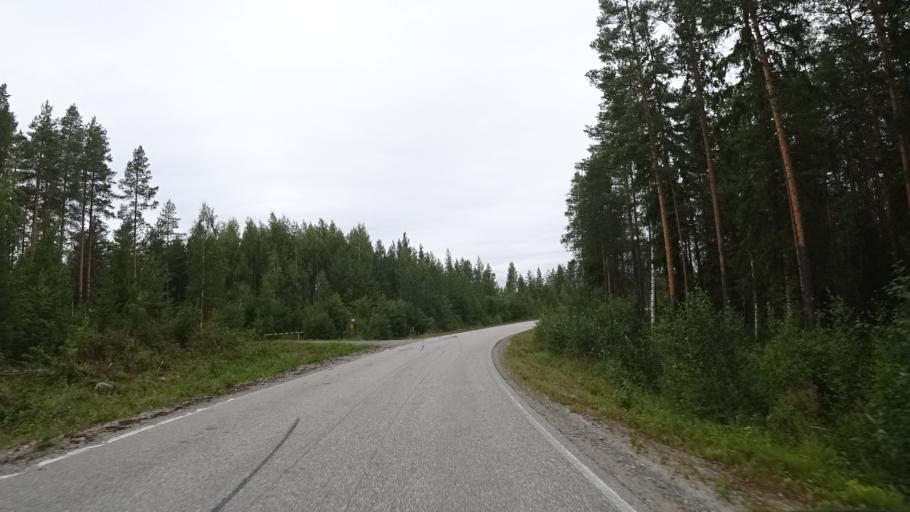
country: FI
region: North Karelia
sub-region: Pielisen Karjala
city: Lieksa
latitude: 63.3571
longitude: 30.2612
